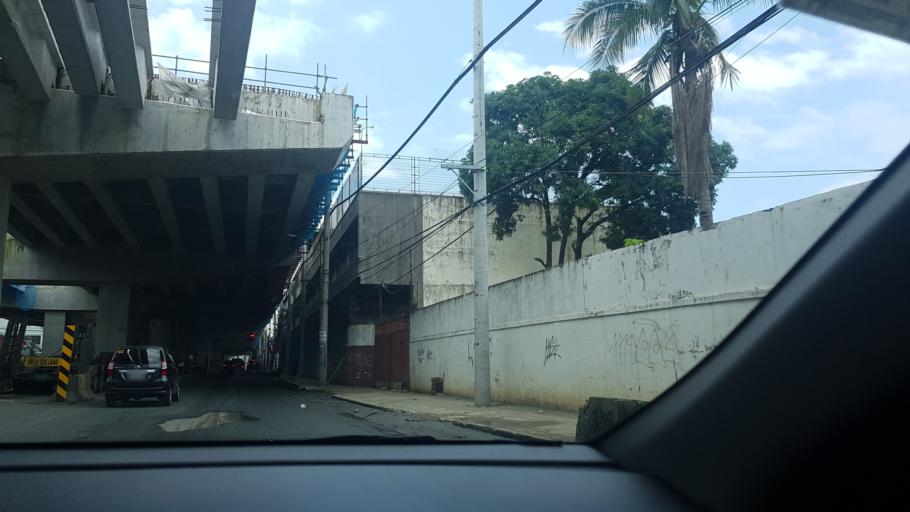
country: PH
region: Calabarzon
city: Del Monte
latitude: 14.6371
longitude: 121.0085
